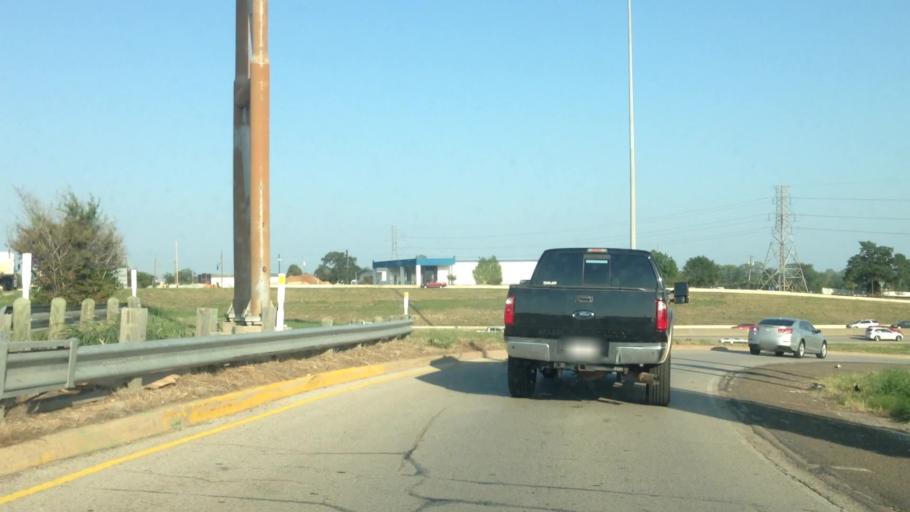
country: US
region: Texas
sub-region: Tarrant County
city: Richland Hills
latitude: 32.8089
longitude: -97.2117
